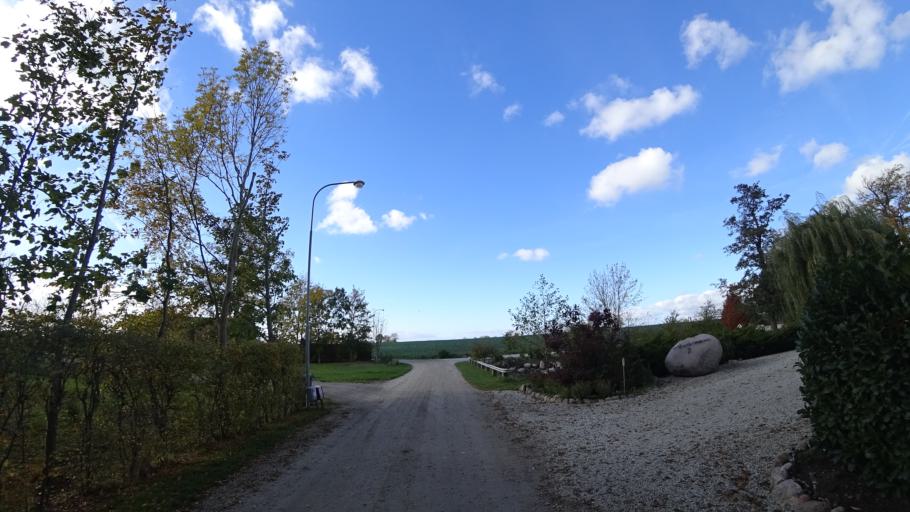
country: SE
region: Skane
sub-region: Staffanstorps Kommun
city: Staffanstorp
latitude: 55.6548
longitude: 13.1975
